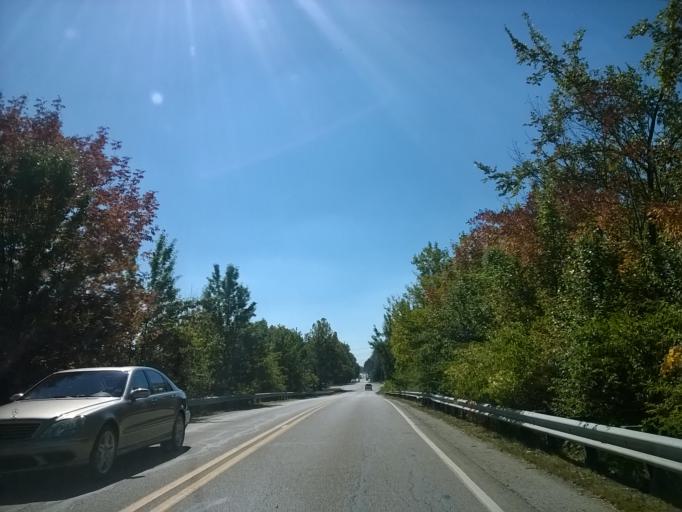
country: US
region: Indiana
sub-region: Marion County
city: Meridian Hills
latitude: 39.9241
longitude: -86.1841
